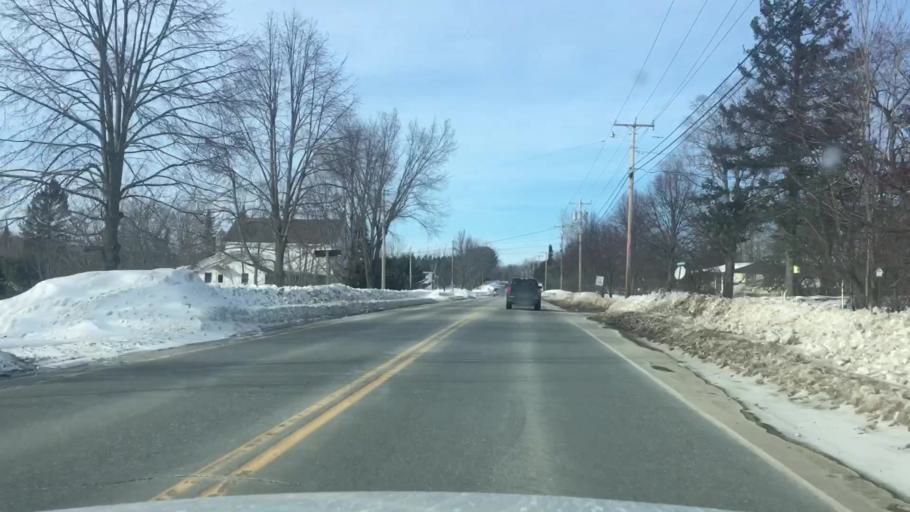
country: US
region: Maine
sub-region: Penobscot County
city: Kenduskeag
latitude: 44.9216
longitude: -68.9319
